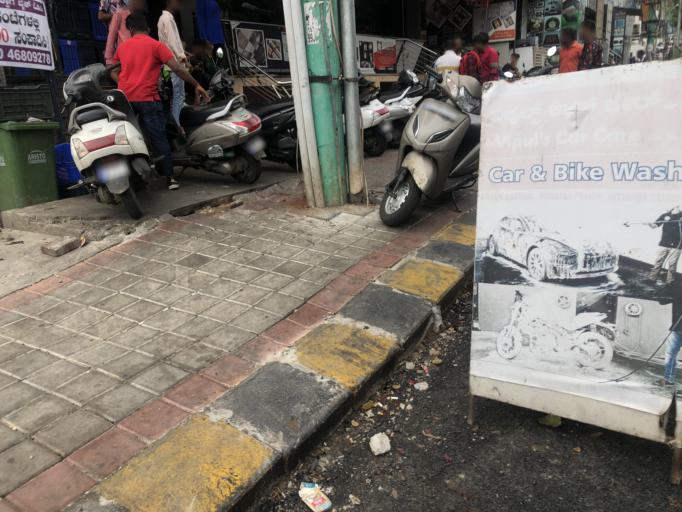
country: IN
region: Karnataka
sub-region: Bangalore Urban
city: Bangalore
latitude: 12.9348
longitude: 77.5470
